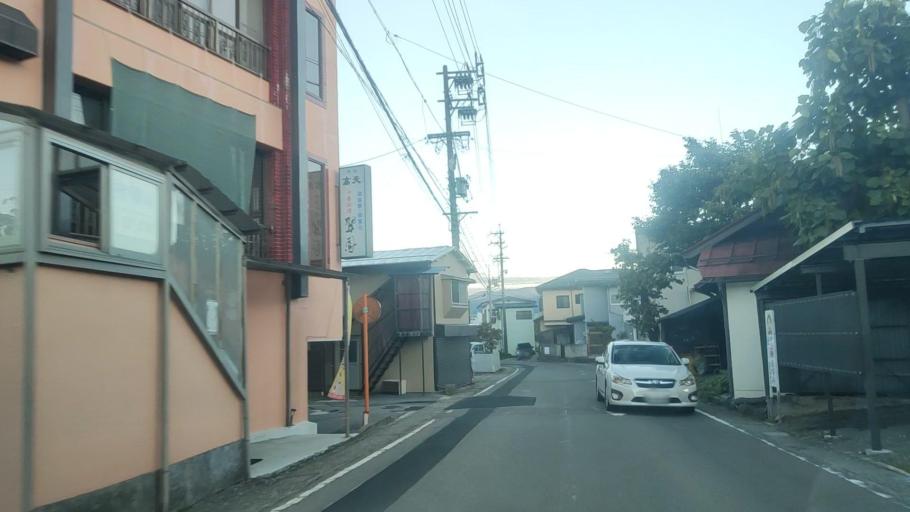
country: JP
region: Nagano
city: Okaya
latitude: 36.0702
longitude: 138.0465
